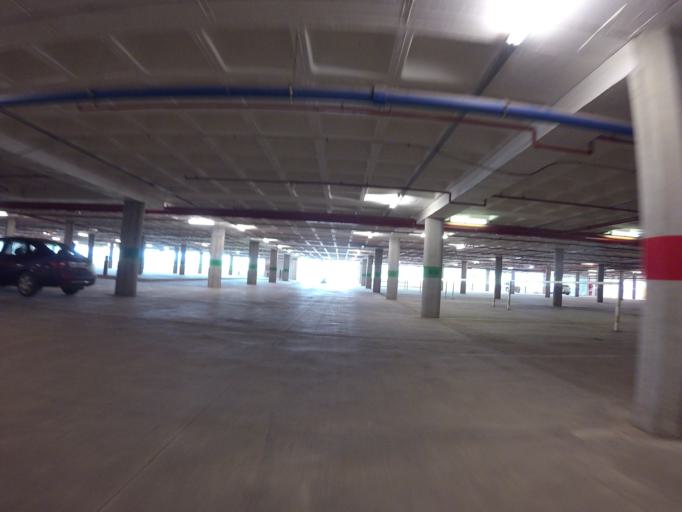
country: GH
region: Greater Accra
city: Gbawe
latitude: 5.5441
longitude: -0.3436
